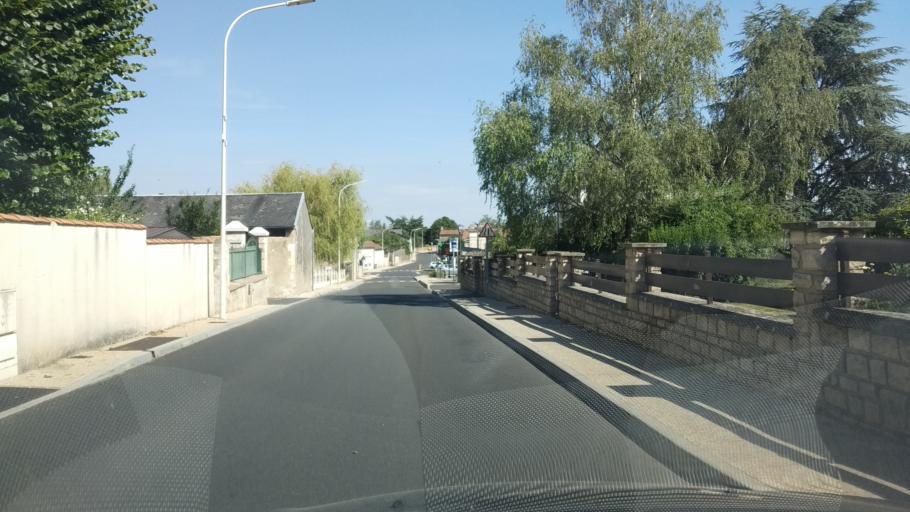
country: FR
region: Poitou-Charentes
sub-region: Departement de la Vienne
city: Cisse
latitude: 46.6469
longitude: 0.2277
